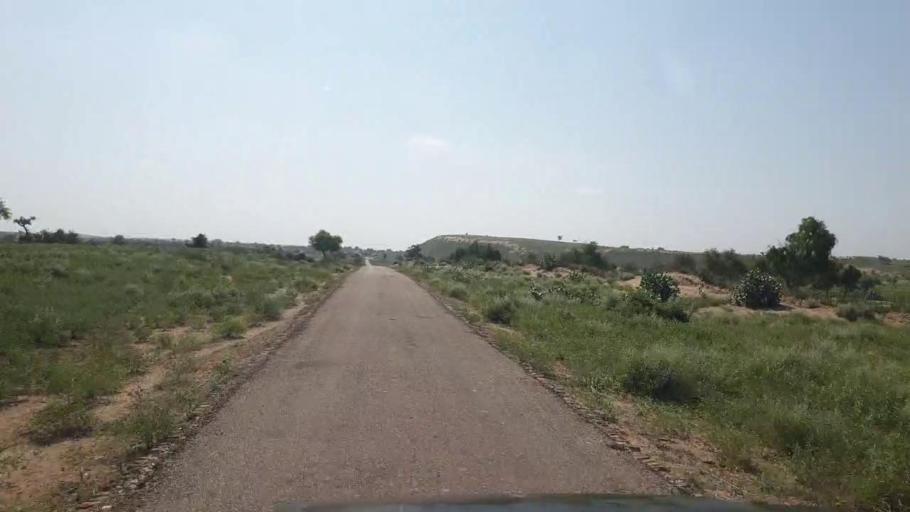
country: PK
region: Sindh
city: Islamkot
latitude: 25.1656
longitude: 70.4031
